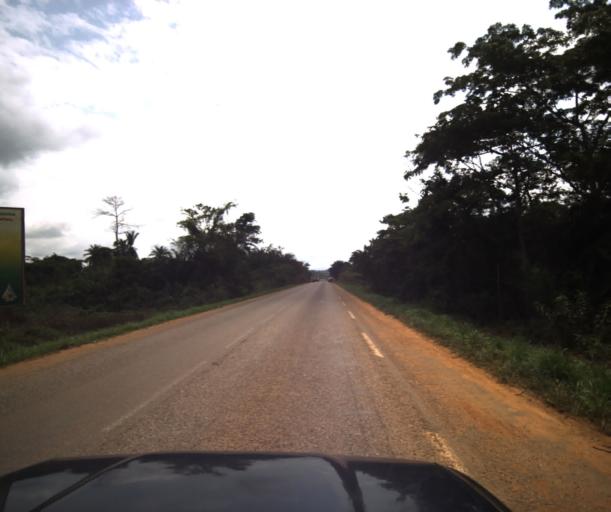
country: CM
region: Centre
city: Eseka
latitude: 3.8534
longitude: 10.5206
